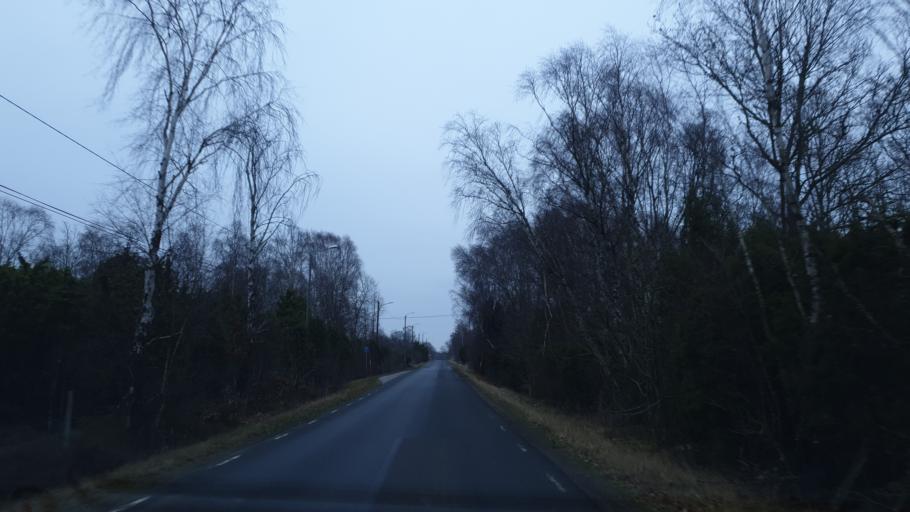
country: SE
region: Blekinge
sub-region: Karlskrona Kommun
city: Karlskrona
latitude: 56.1116
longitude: 15.6137
